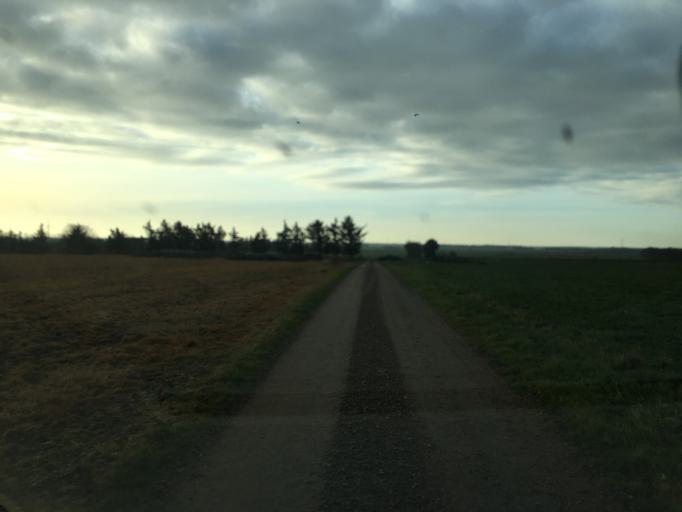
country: DK
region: South Denmark
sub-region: Tonder Kommune
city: Logumkloster
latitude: 55.1124
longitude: 8.8657
